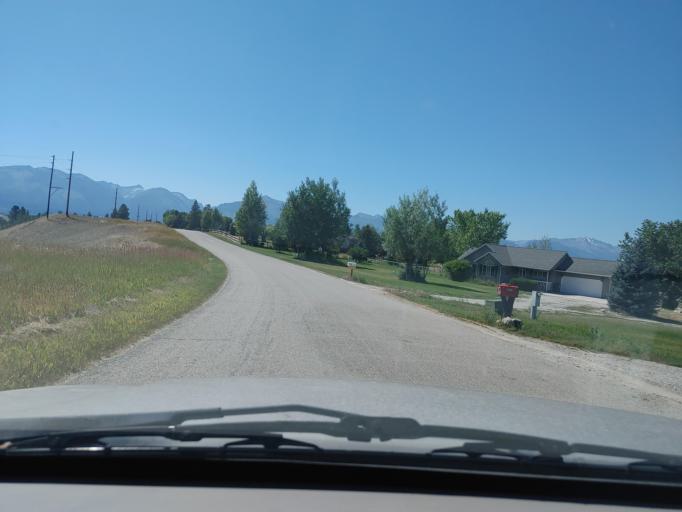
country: US
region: Montana
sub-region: Ravalli County
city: Hamilton
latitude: 46.2773
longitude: -114.0407
